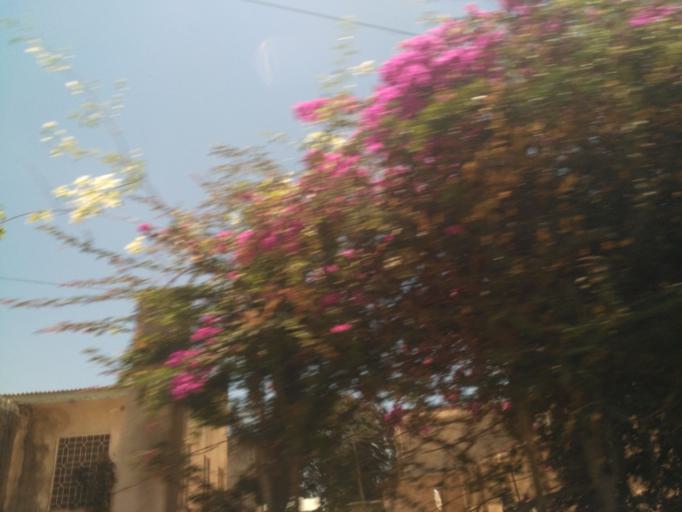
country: TZ
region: Dodoma
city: Dodoma
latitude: -6.1643
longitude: 35.7449
